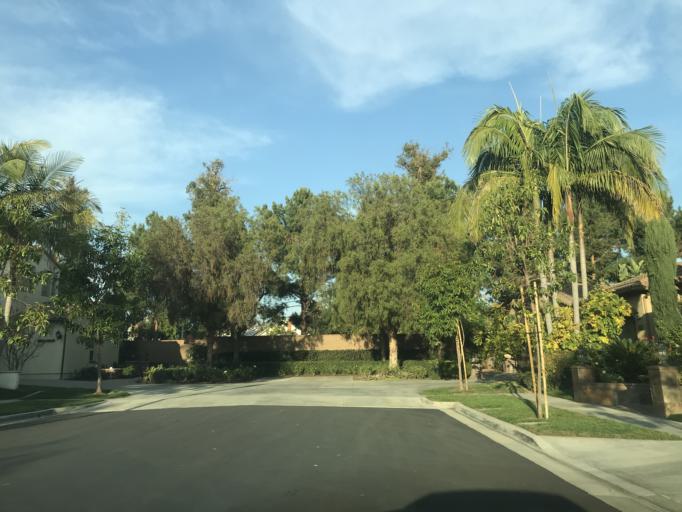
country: US
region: California
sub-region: Orange County
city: North Tustin
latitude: 33.7031
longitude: -117.7591
